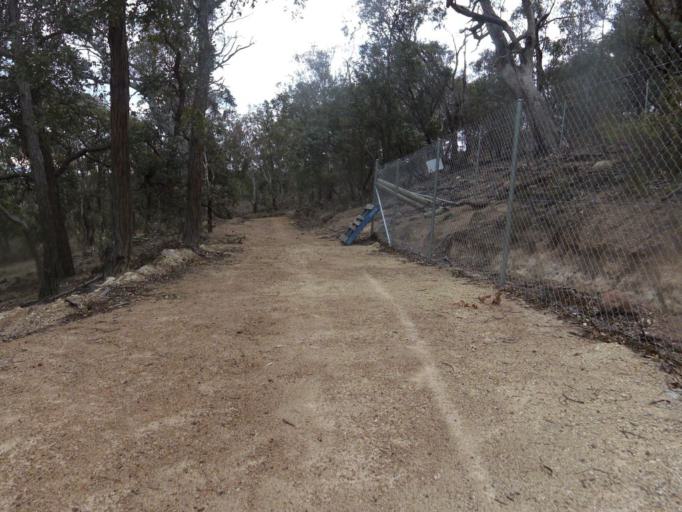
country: AU
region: Australian Capital Territory
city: Forrest
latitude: -35.3514
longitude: 149.1239
